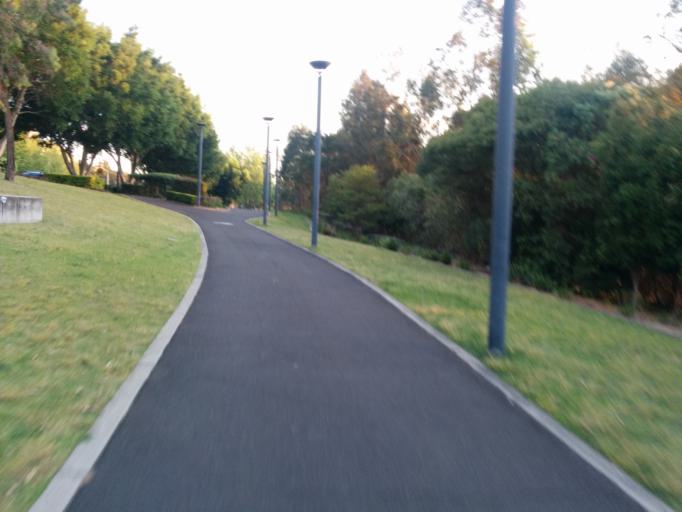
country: AU
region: New South Wales
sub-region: Canada Bay
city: Rhodes
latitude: -33.8353
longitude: 151.0837
